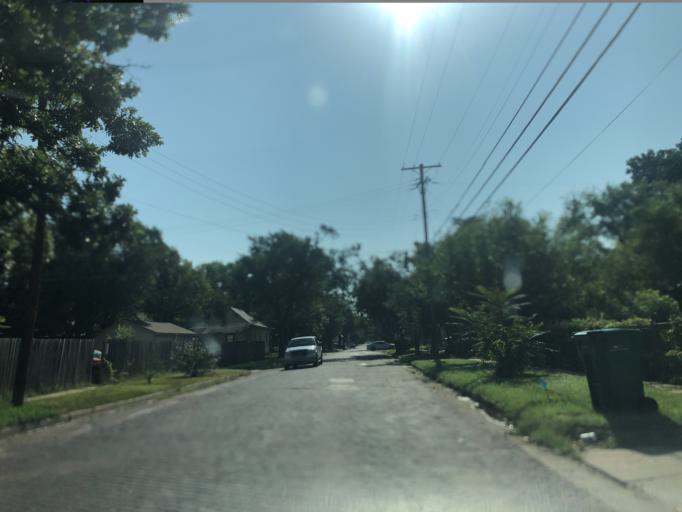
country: US
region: Kansas
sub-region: Sedgwick County
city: Wichita
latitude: 37.7171
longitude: -97.3445
